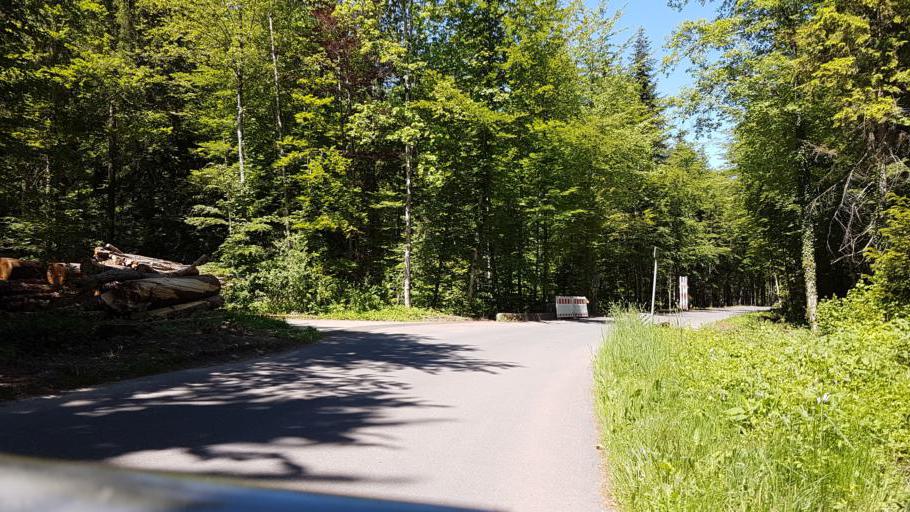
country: CH
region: Bern
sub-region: Thun District
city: Thun
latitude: 46.7243
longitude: 7.6021
